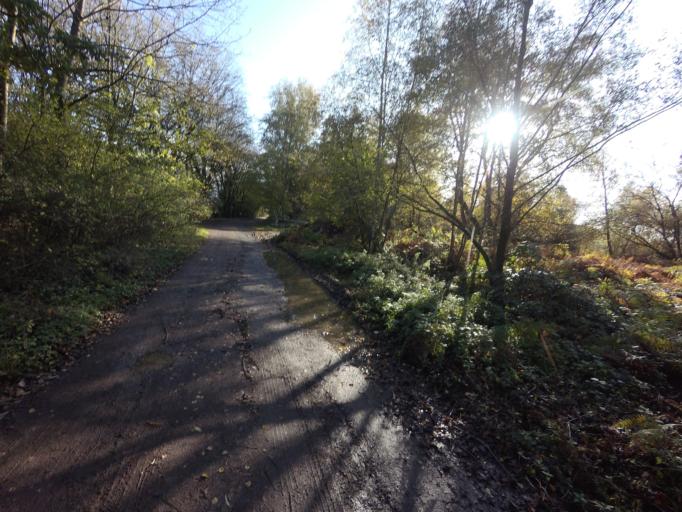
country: BE
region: Wallonia
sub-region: Province de Liege
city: Aubel
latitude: 50.7584
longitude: 5.8876
